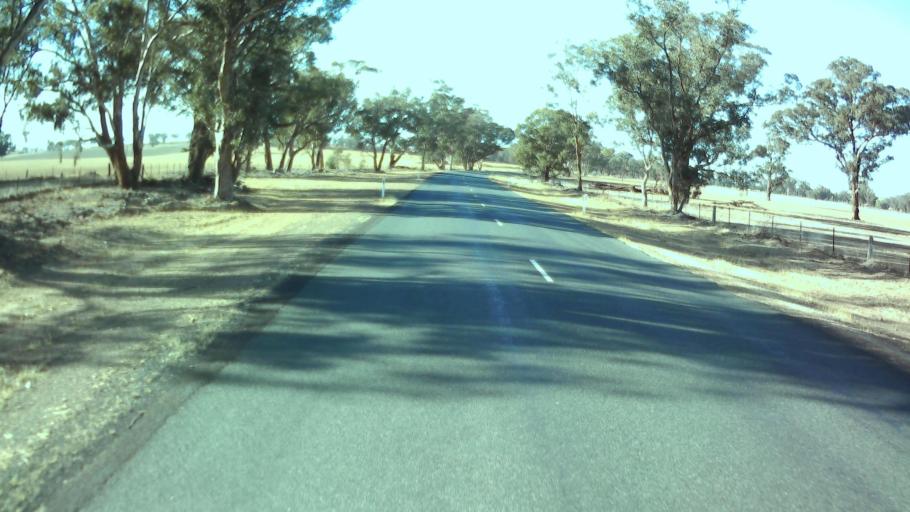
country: AU
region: New South Wales
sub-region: Weddin
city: Grenfell
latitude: -33.9332
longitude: 148.1376
